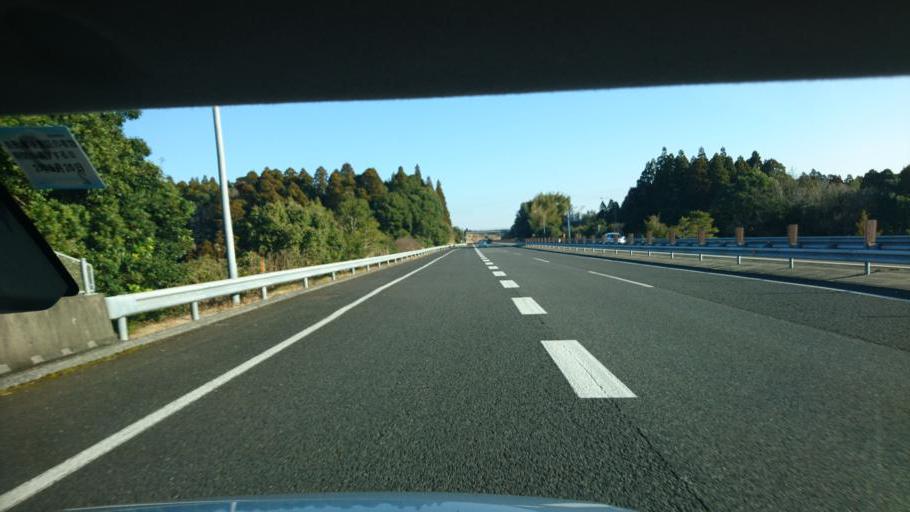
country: JP
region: Miyazaki
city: Miyazaki-shi
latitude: 31.8683
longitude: 131.3589
